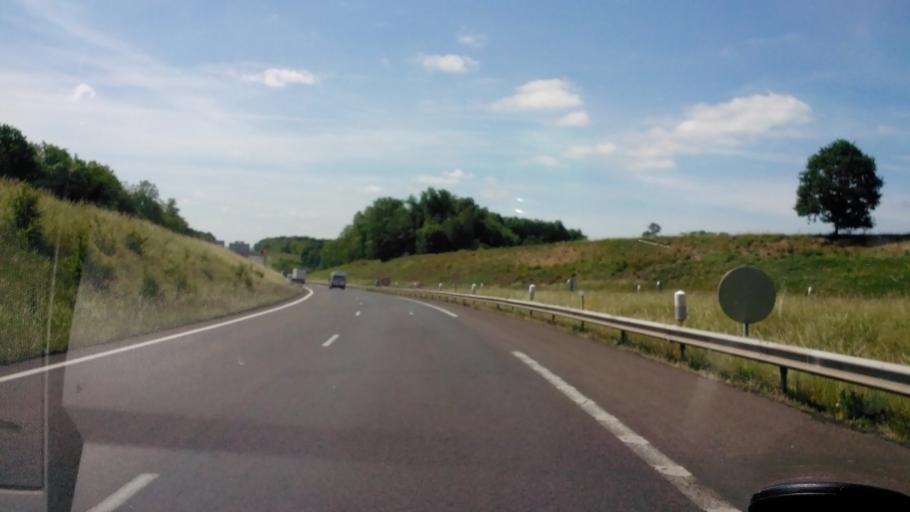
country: FR
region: Lorraine
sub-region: Departement de Meurthe-et-Moselle
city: Dommartin-les-Toul
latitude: 48.6508
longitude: 5.8802
